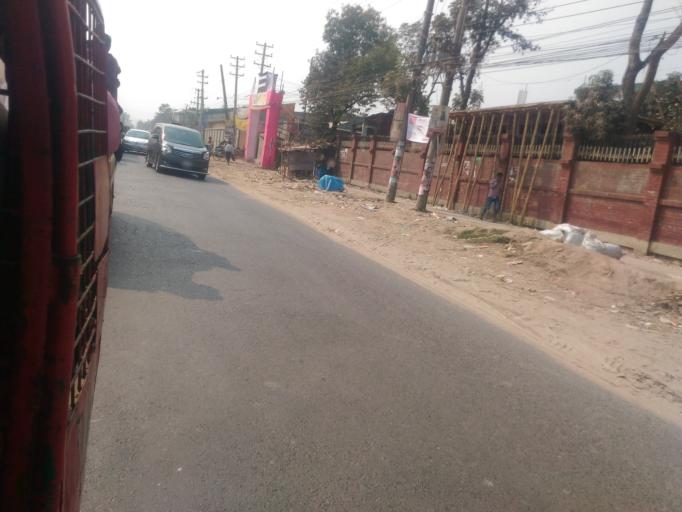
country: BD
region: Dhaka
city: Tungi
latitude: 23.9931
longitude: 90.4050
